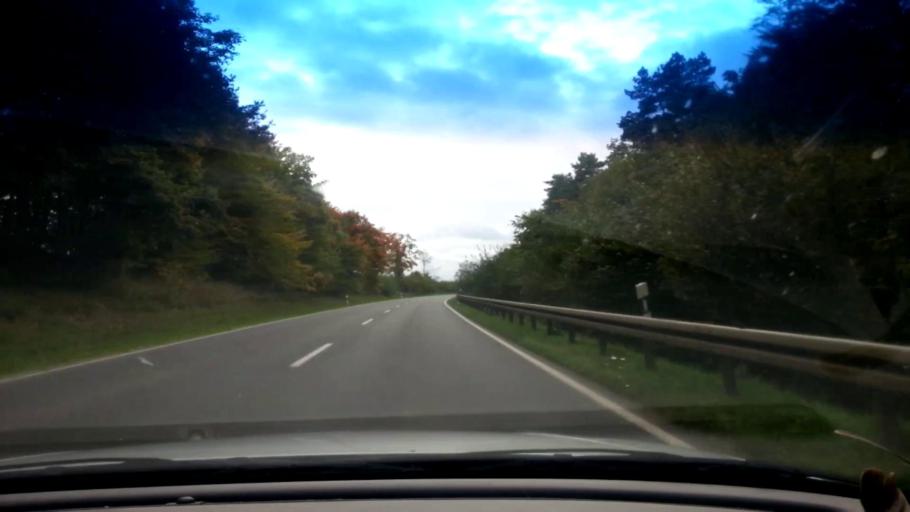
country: DE
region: Bavaria
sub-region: Upper Franconia
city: Viereth-Trunstadt
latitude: 49.9053
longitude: 10.7951
